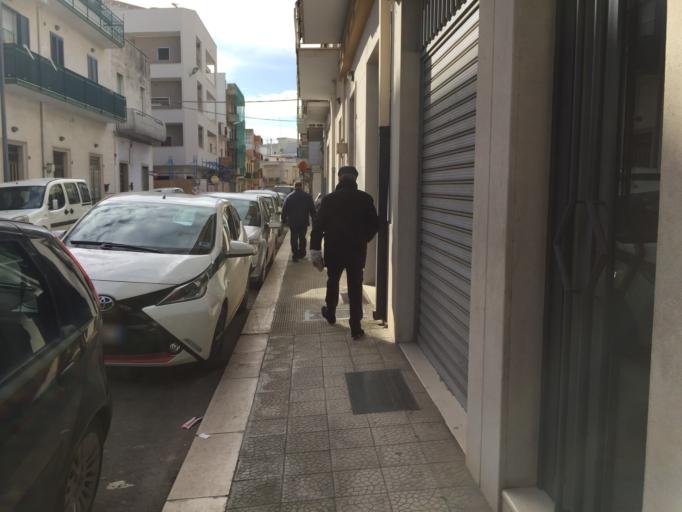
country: IT
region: Apulia
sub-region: Provincia di Barletta - Andria - Trani
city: Andria
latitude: 41.2243
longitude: 16.3057
